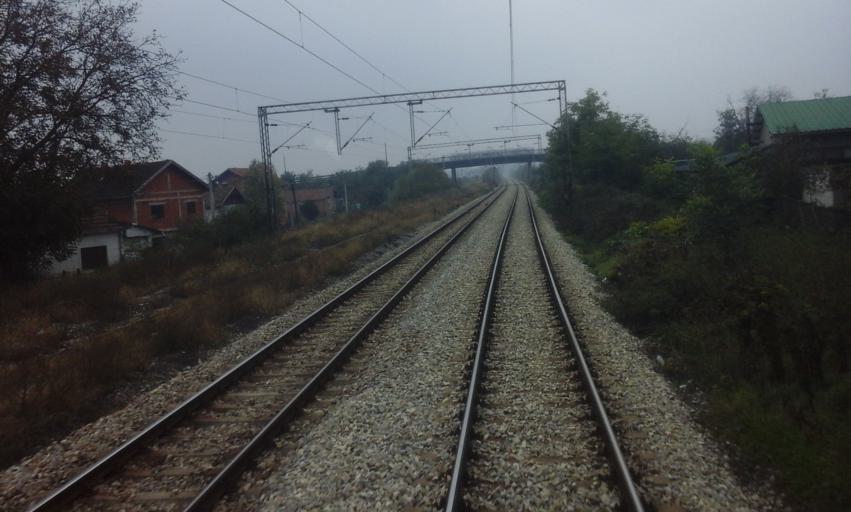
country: RS
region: Central Serbia
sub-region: Sumadijski Okrug
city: Lapovo
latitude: 44.1828
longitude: 21.1028
